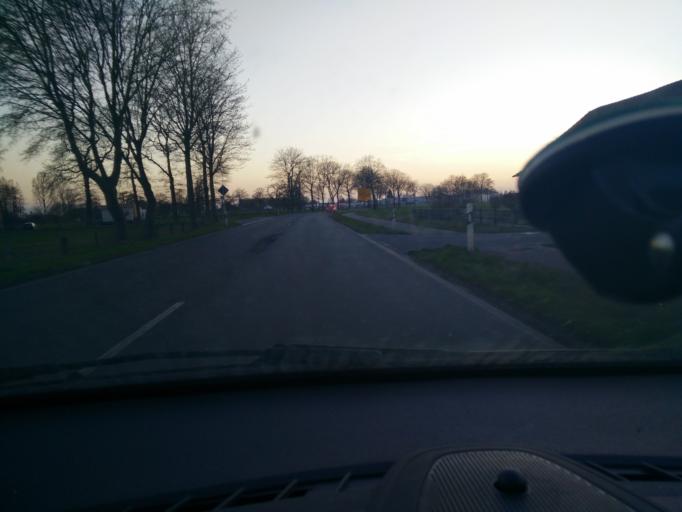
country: DE
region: North Rhine-Westphalia
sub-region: Regierungsbezirk Munster
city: Rhede
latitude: 51.7334
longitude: 6.6985
